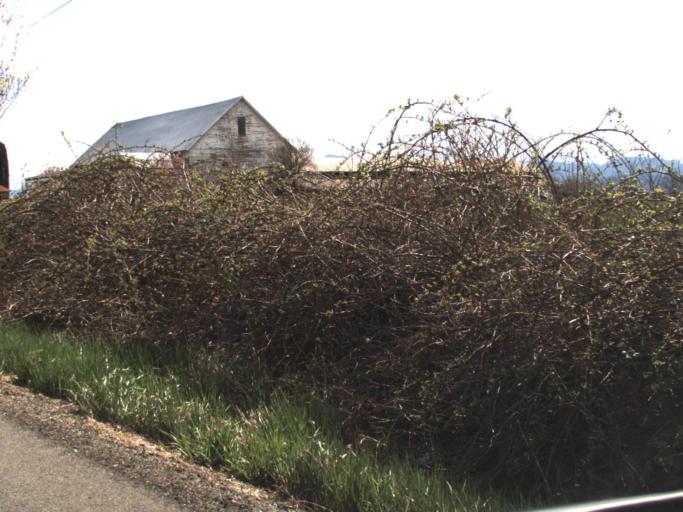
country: US
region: Washington
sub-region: Pierce County
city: Buckley
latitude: 47.2102
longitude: -122.0754
